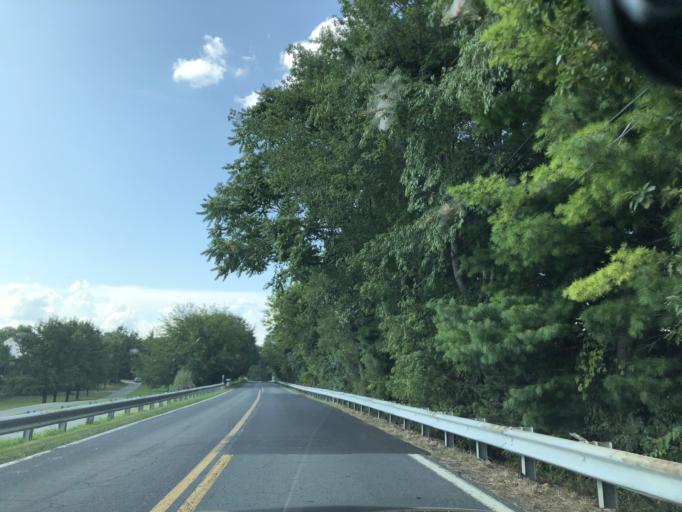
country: US
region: Maryland
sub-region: Carroll County
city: Mount Airy
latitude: 39.4024
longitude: -77.1783
